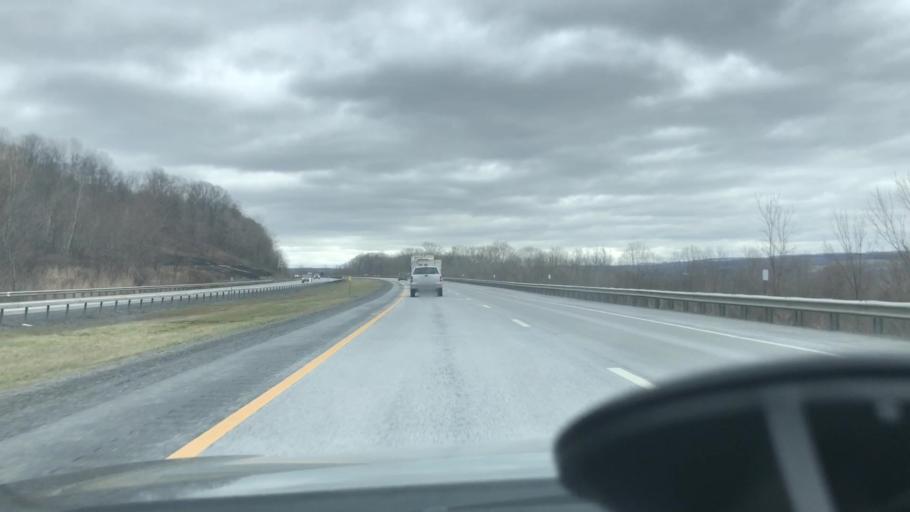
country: US
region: New York
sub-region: Herkimer County
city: Ilion
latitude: 43.0324
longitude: -75.0450
